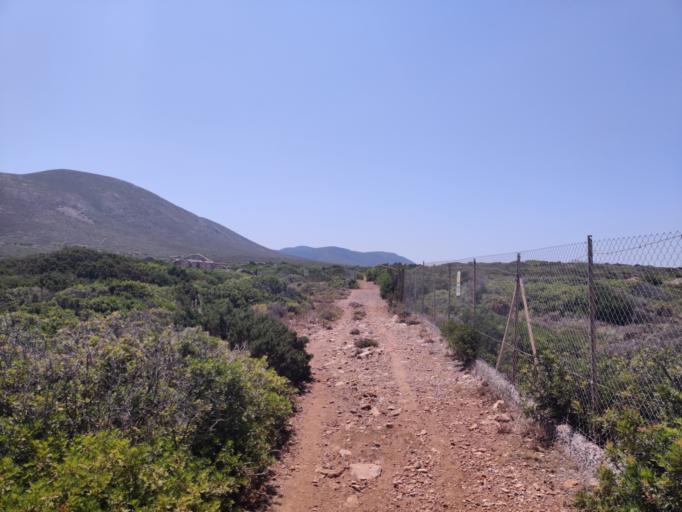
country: IT
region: Sardinia
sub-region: Provincia di Carbonia-Iglesias
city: Buggerru
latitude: 39.3931
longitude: 8.3885
